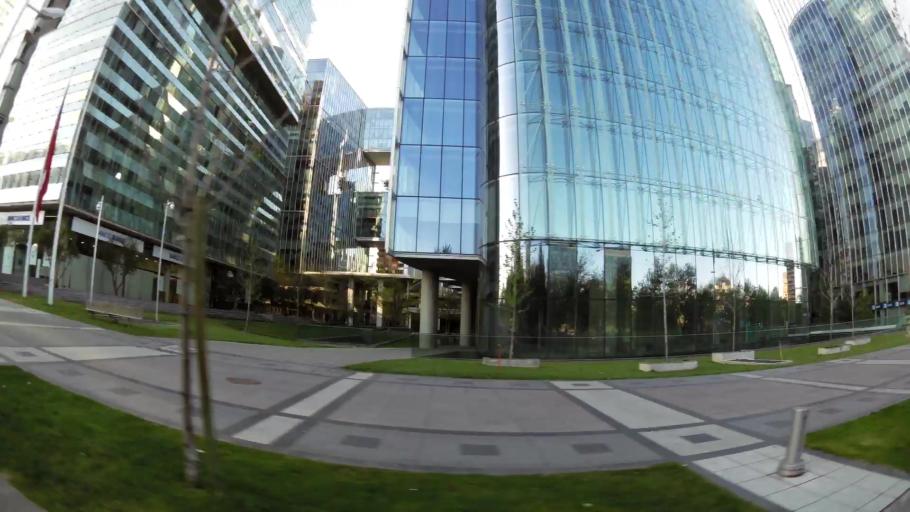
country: CL
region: Santiago Metropolitan
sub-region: Provincia de Santiago
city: Villa Presidente Frei, Nunoa, Santiago, Chile
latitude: -33.4050
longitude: -70.5747
